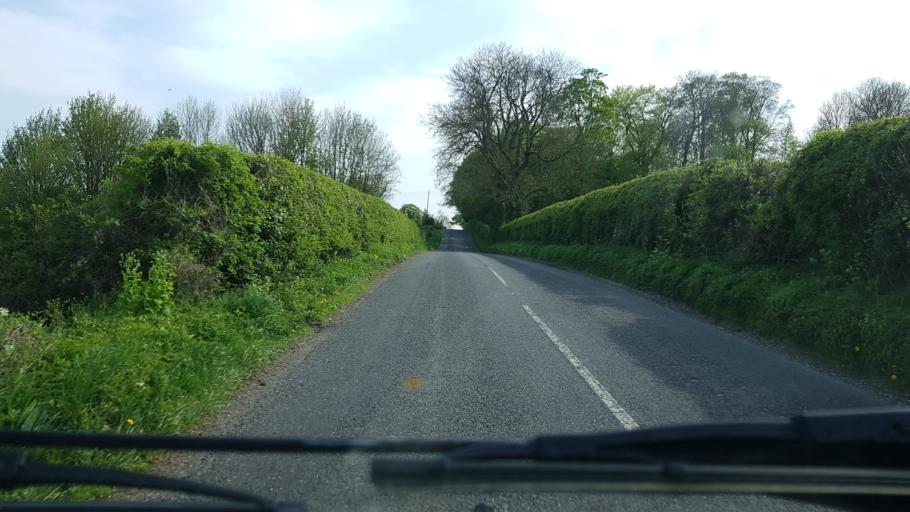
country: GB
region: England
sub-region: Hampshire
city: Overton
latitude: 51.2768
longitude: -1.2630
